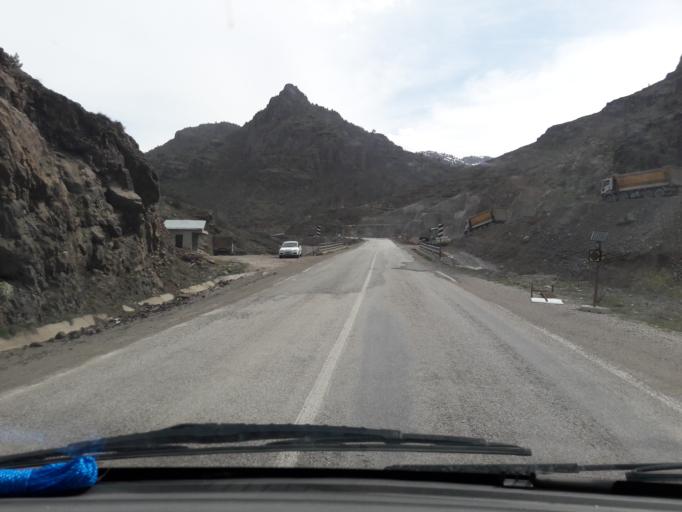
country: TR
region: Gumushane
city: Gumushkhane
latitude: 40.3020
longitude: 39.4743
